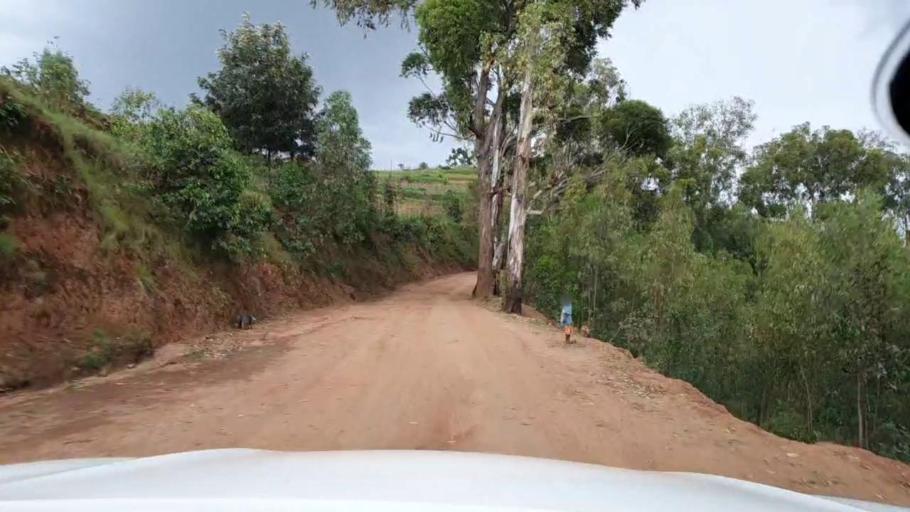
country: BI
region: Kayanza
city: Kayanza
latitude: -2.7899
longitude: 29.5260
